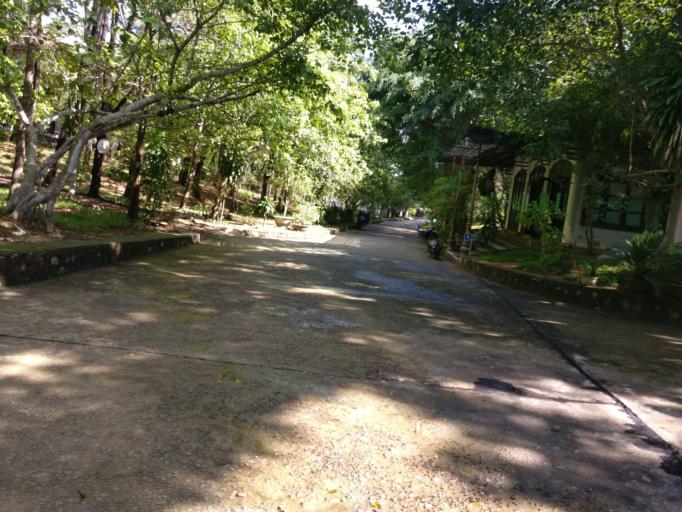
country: VN
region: Thua Thien-Hue
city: Hue
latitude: 16.4194
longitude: 107.6079
